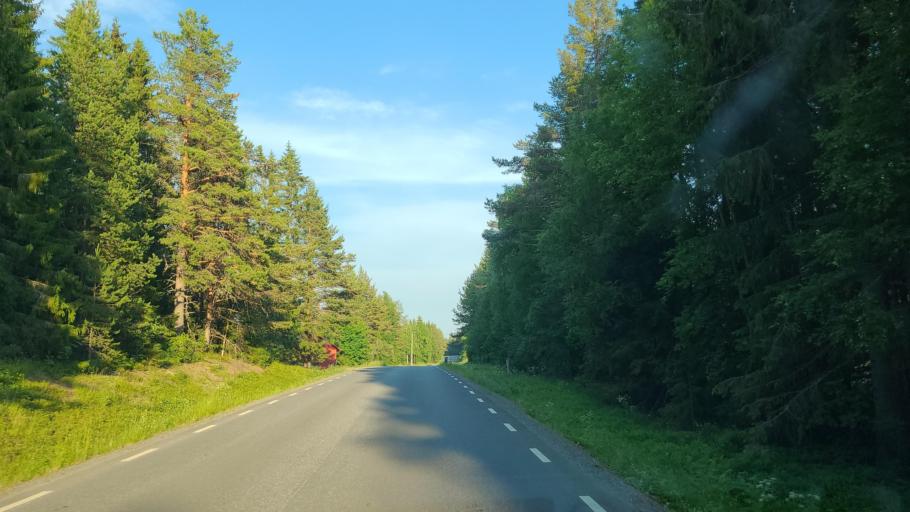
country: SE
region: Vaesterbotten
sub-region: Skelleftea Kommun
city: Burea
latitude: 64.4452
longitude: 21.4805
